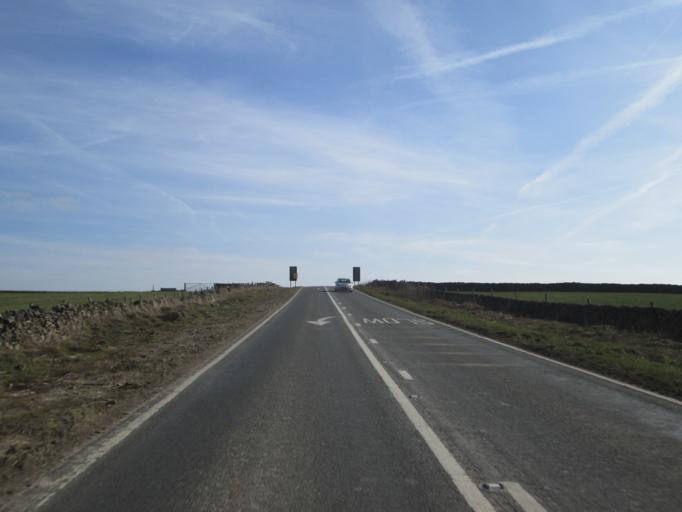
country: GB
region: England
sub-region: Derbyshire
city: Tideswell
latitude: 53.1676
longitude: -1.7784
